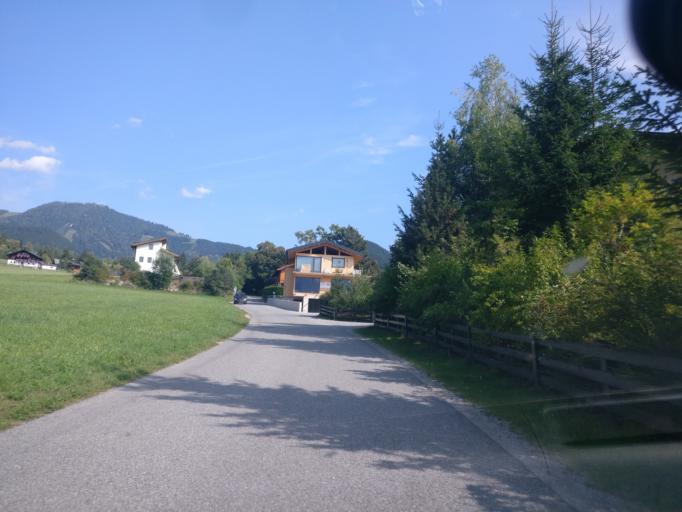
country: AT
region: Salzburg
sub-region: Politischer Bezirk Sankt Johann im Pongau
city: Werfenweng
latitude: 47.4632
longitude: 13.2324
